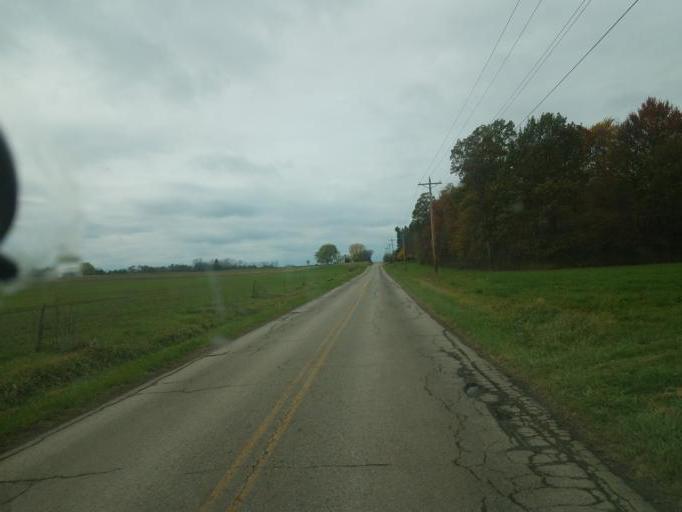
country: US
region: Ohio
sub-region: Wayne County
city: Shreve
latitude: 40.6245
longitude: -82.0791
